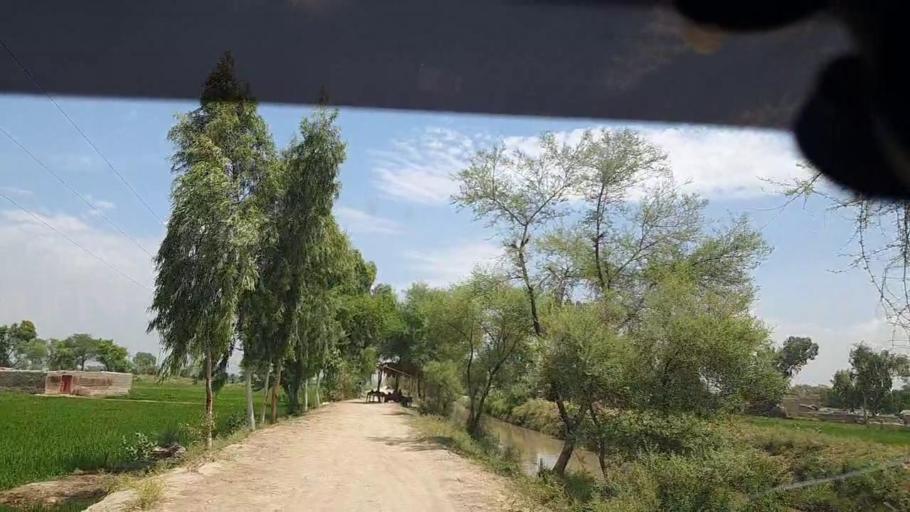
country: PK
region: Sindh
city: Ghauspur
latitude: 28.1047
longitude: 68.9874
